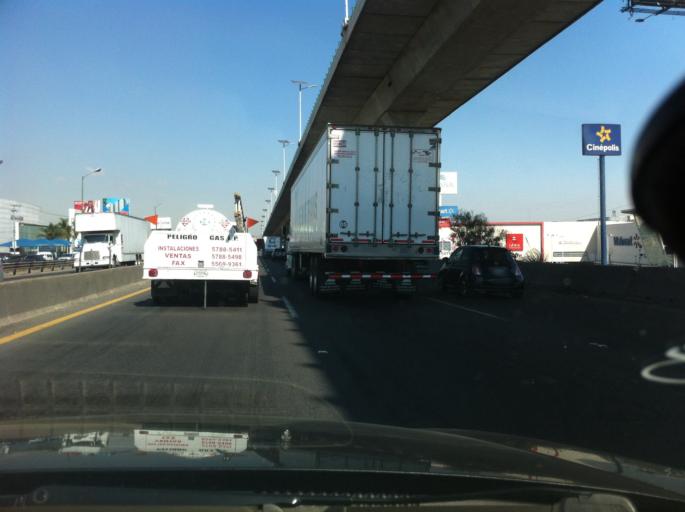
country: MX
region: Mexico
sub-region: Tultitlan
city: Buenavista
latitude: 19.6041
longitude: -99.1890
